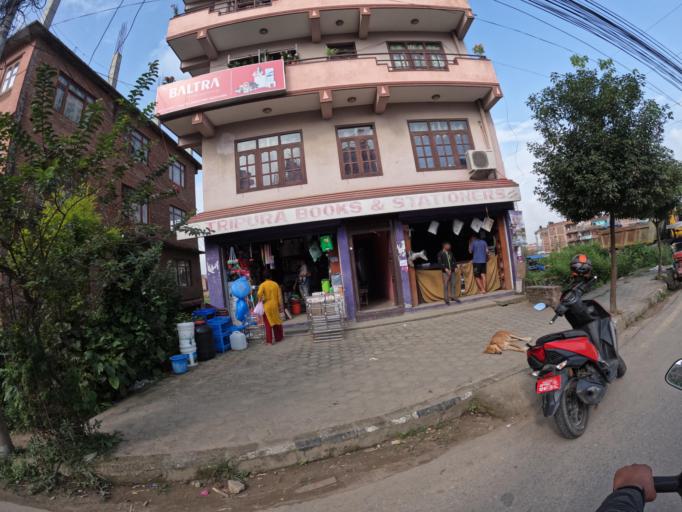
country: NP
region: Central Region
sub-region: Bagmati Zone
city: Bhaktapur
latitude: 27.6766
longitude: 85.4296
